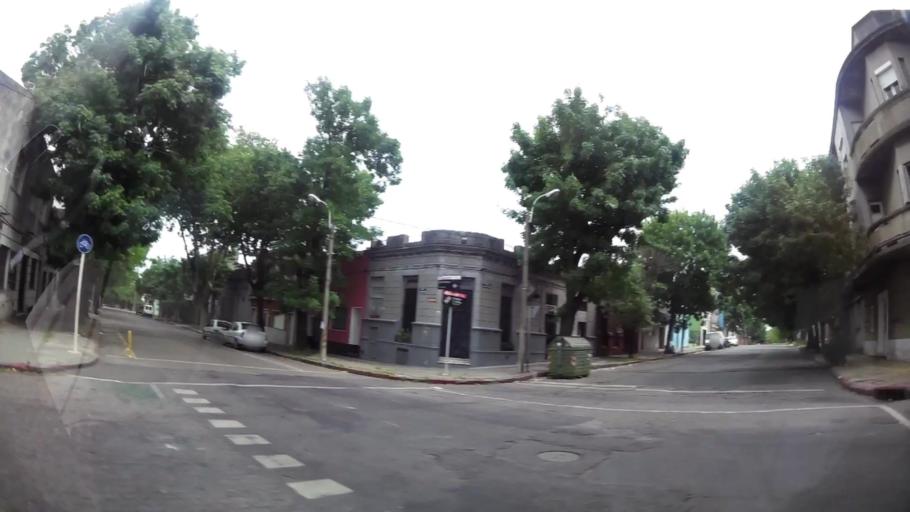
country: UY
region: Montevideo
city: Montevideo
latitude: -34.8887
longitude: -56.1736
